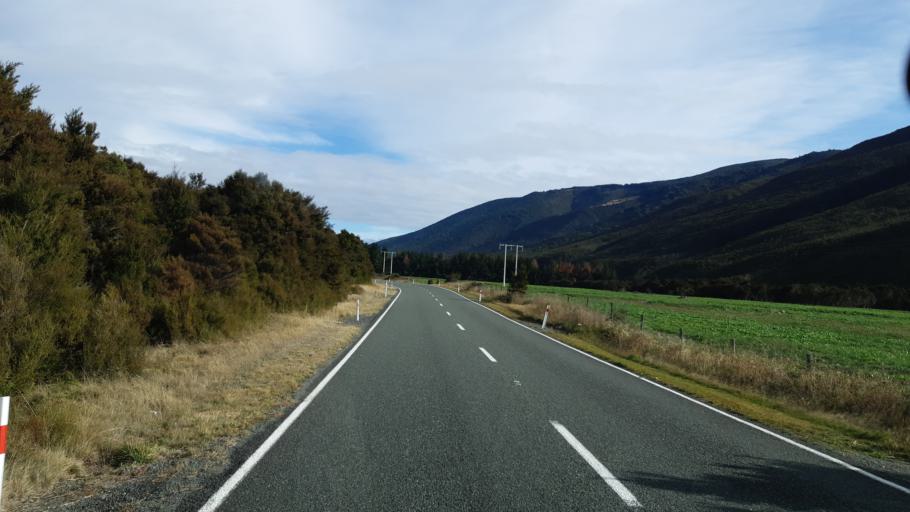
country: NZ
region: Tasman
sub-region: Tasman District
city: Wakefield
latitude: -41.7399
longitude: 173.0141
